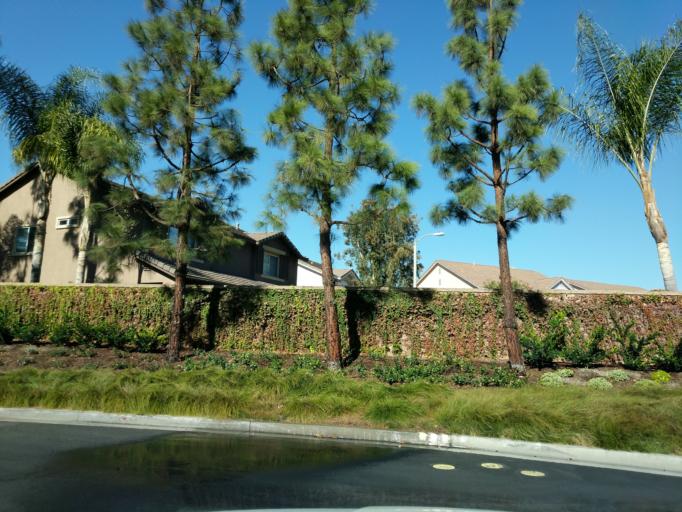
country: US
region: California
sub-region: Orange County
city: Tustin
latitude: 33.7119
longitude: -117.7960
